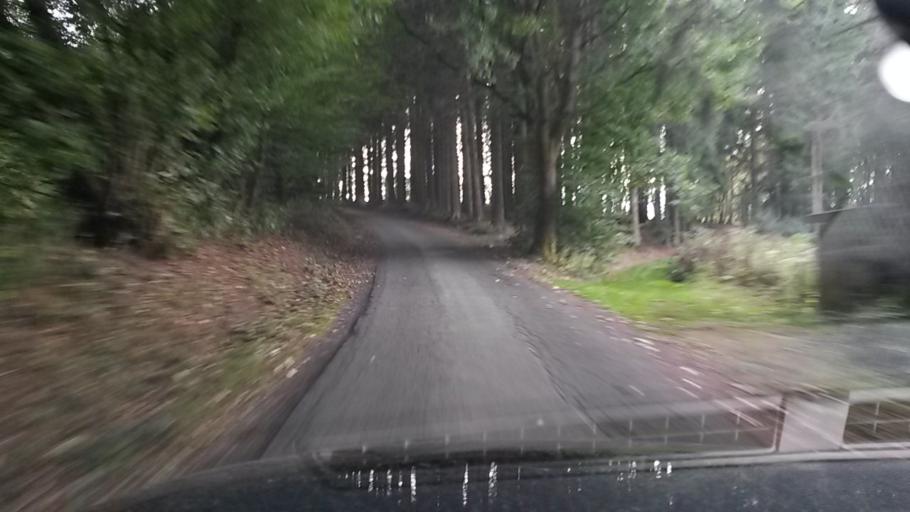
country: DE
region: North Rhine-Westphalia
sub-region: Regierungsbezirk Arnsberg
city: Herscheid
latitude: 51.2055
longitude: 7.7568
